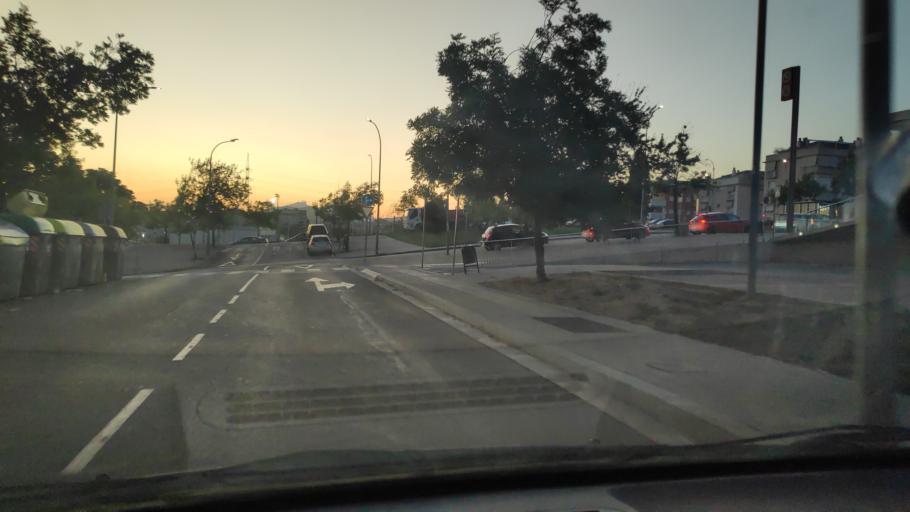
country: ES
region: Catalonia
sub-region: Provincia de Barcelona
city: Terrassa
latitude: 41.5672
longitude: 2.0396
